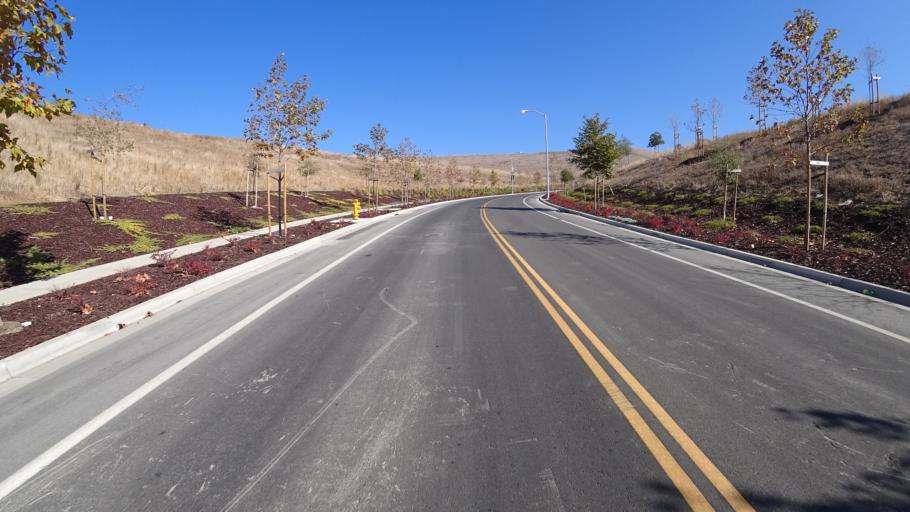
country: US
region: California
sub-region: Alameda County
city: Fairview
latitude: 37.6372
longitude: -122.0495
